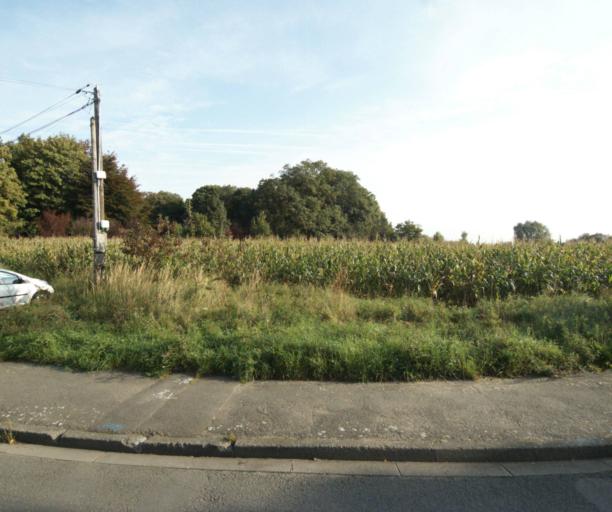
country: FR
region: Nord-Pas-de-Calais
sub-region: Departement du Nord
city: Lomme
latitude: 50.6535
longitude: 2.9940
